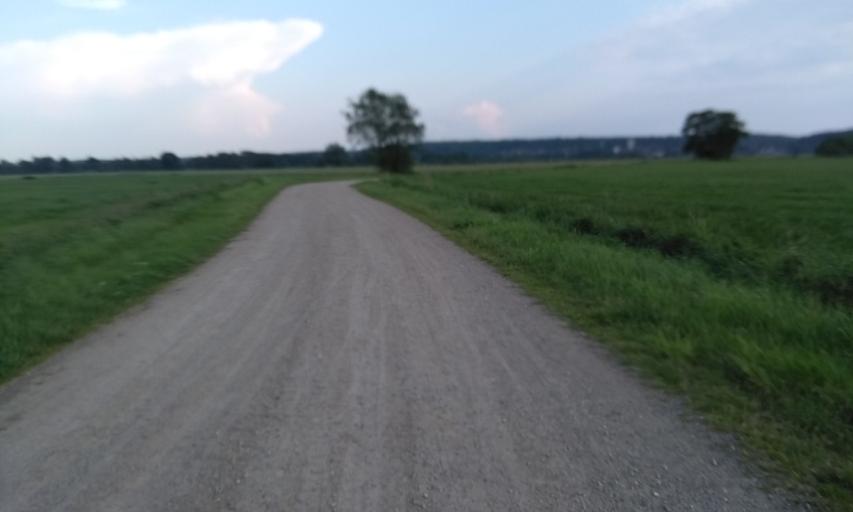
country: DE
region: Lower Saxony
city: Nottensdorf
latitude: 53.4945
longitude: 9.6388
